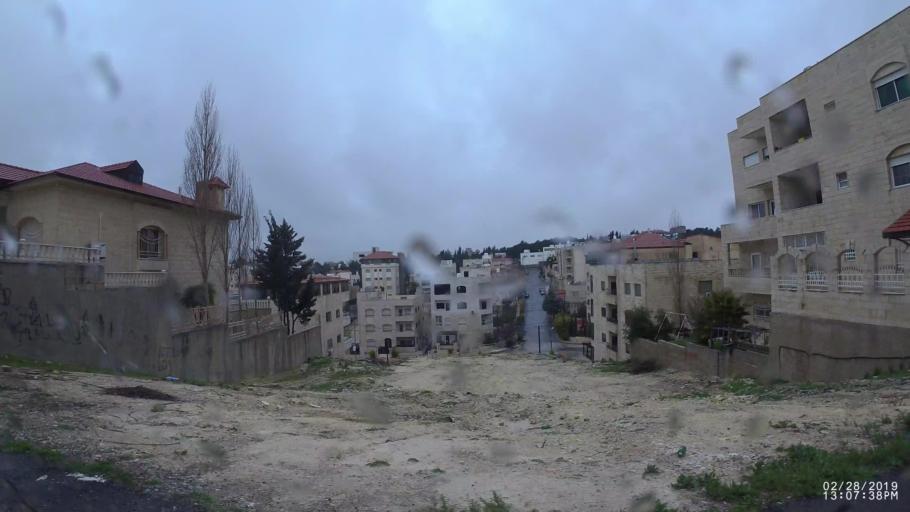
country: JO
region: Amman
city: Al Jubayhah
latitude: 32.0238
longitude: 35.8826
